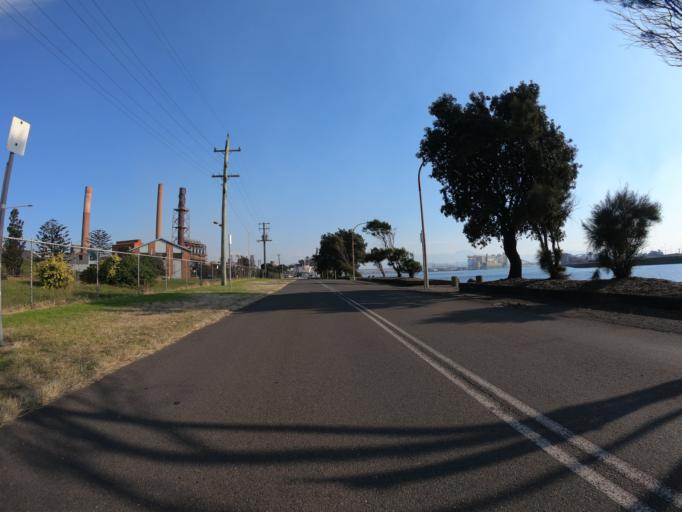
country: AU
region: New South Wales
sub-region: Wollongong
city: Cringila
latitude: -34.4647
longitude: 150.8993
